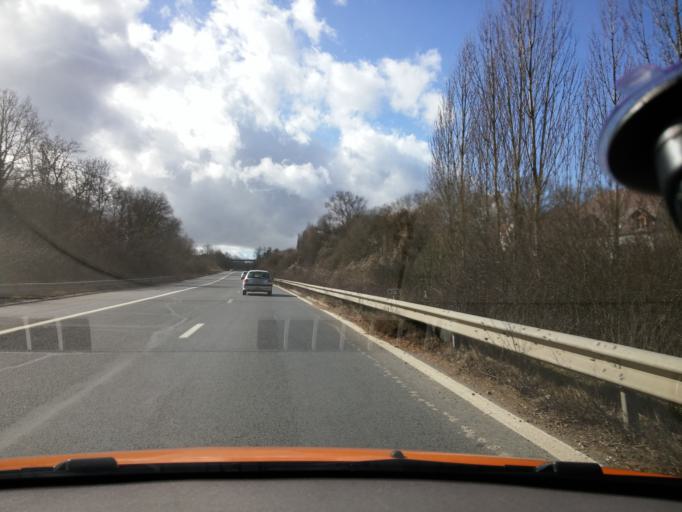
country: FR
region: Ile-de-France
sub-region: Departement de l'Essonne
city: Palaiseau
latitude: 48.7240
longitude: 2.2372
